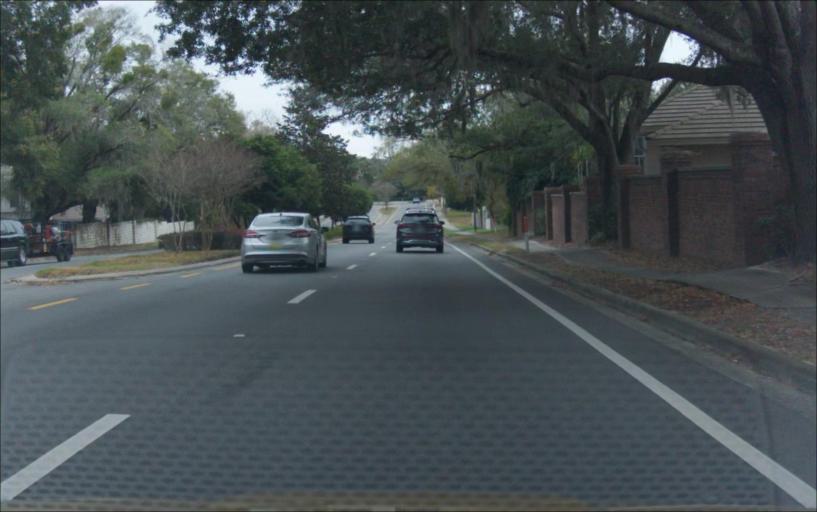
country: US
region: Florida
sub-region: Orange County
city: Winter Park
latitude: 28.6243
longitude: -81.3264
